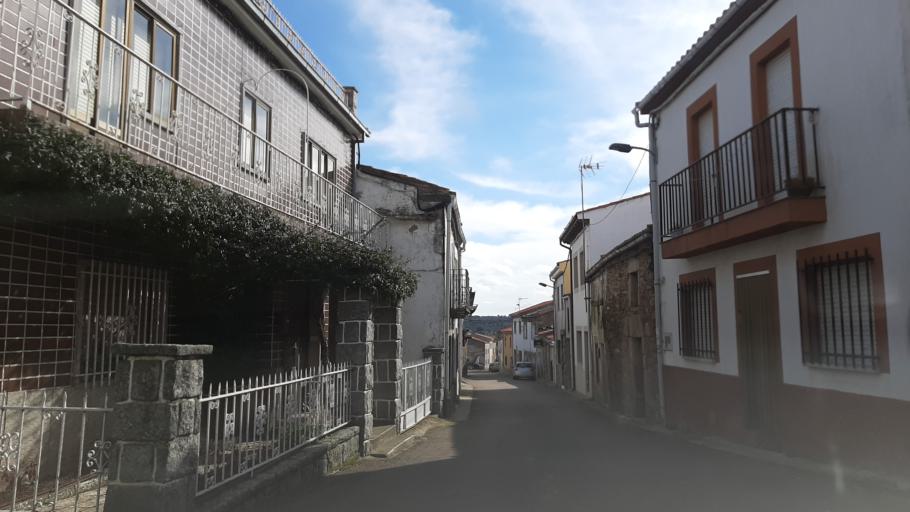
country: ES
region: Castille and Leon
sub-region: Provincia de Salamanca
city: Villarino de los Aires
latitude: 41.2402
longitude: -6.5233
